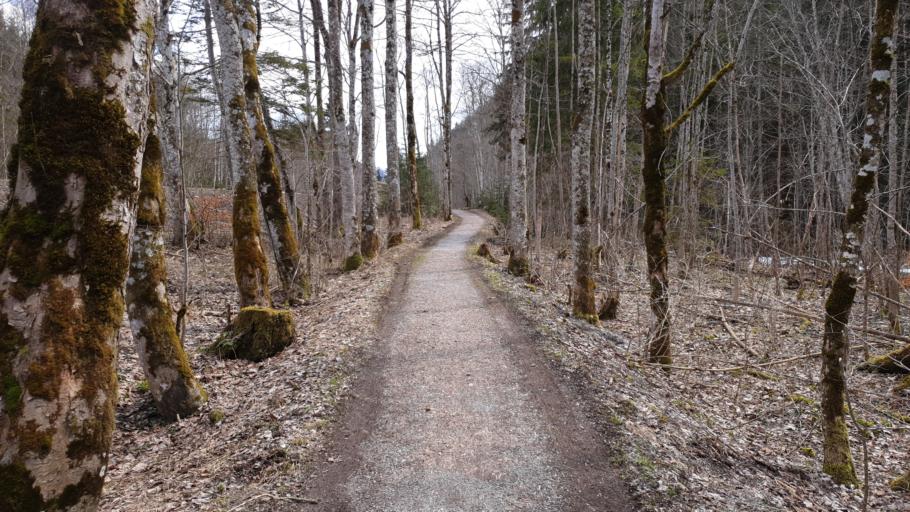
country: DE
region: Bavaria
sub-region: Upper Bavaria
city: Bayrischzell
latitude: 47.6460
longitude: 12.0084
